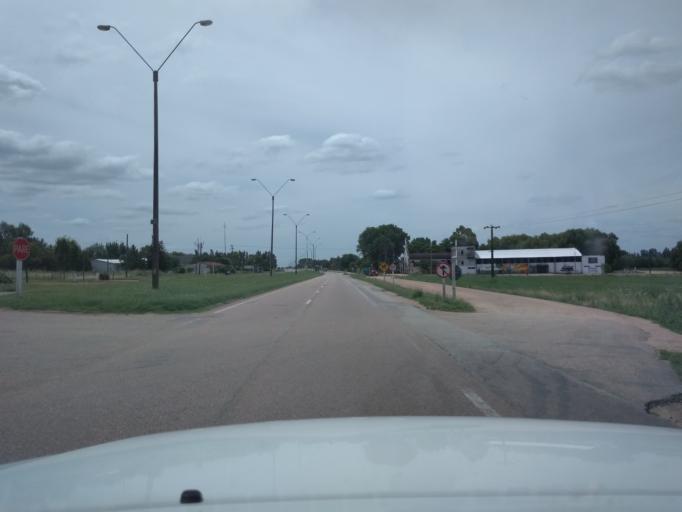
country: UY
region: Canelones
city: Joanico
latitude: -34.5956
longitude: -56.2620
